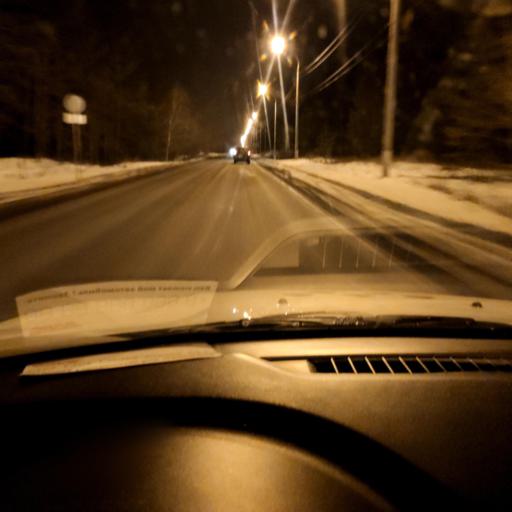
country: RU
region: Samara
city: Tol'yatti
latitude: 53.4763
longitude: 49.4236
